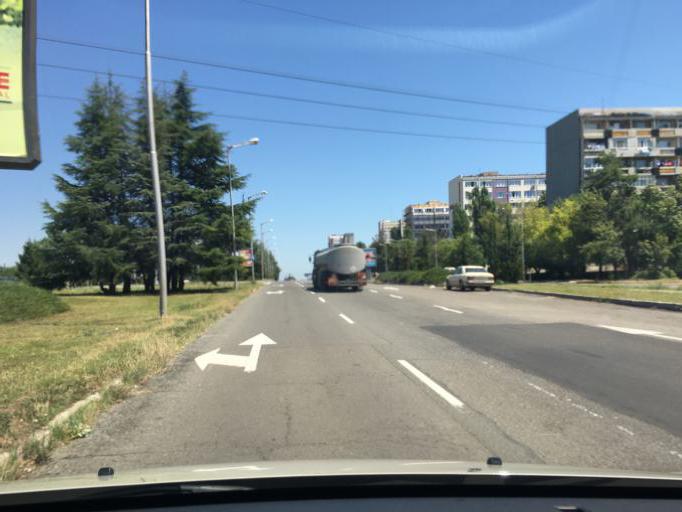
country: BG
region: Burgas
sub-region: Obshtina Burgas
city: Burgas
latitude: 42.5234
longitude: 27.4452
